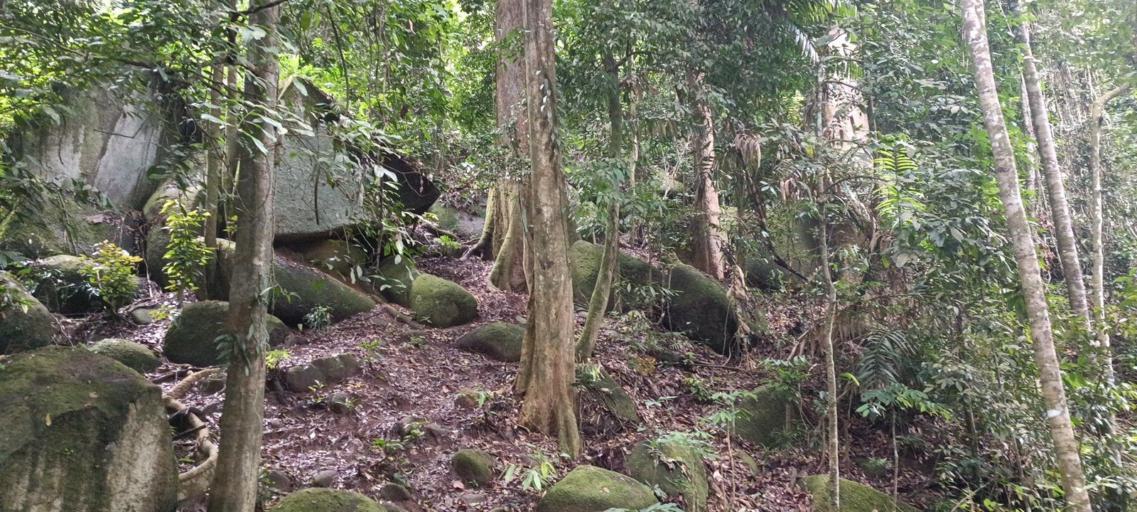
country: MY
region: Penang
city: Bukit Mertajam
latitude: 5.3631
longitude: 100.4844
